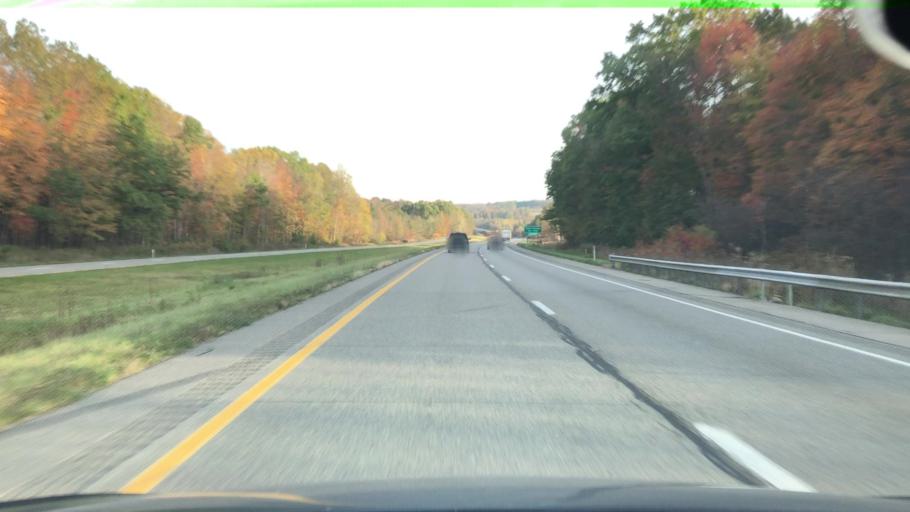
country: US
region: Pennsylvania
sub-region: Mercer County
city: Stoneboro
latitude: 41.3563
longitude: -80.1595
